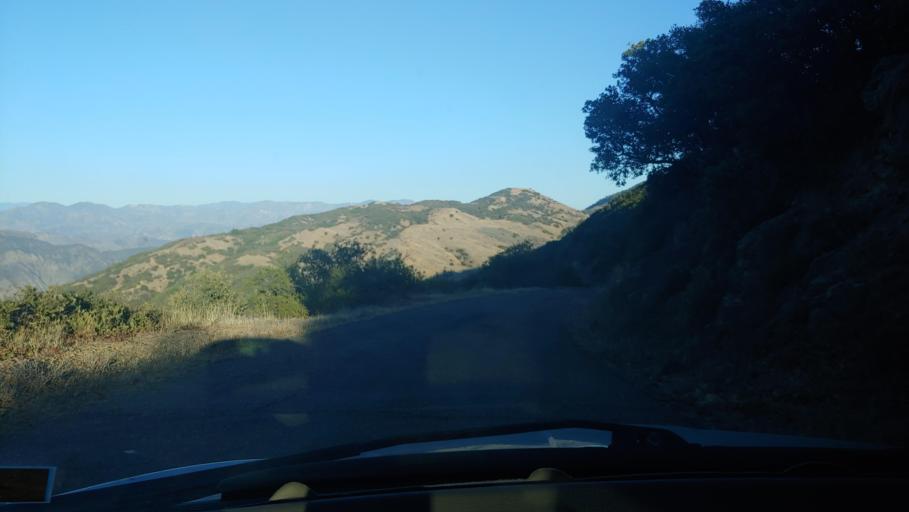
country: US
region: California
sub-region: Santa Barbara County
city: Mission Canyon
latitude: 34.5069
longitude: -119.7604
